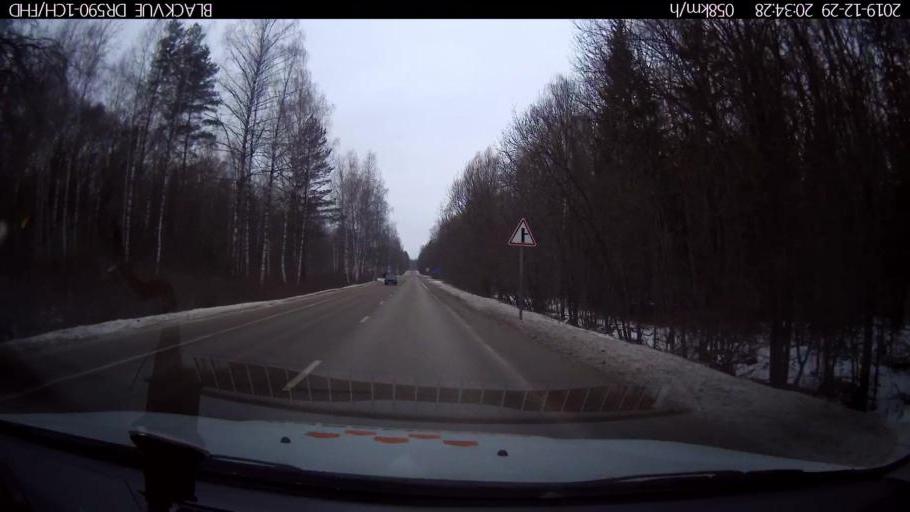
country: RU
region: Nizjnij Novgorod
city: Afonino
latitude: 56.1861
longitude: 44.0393
